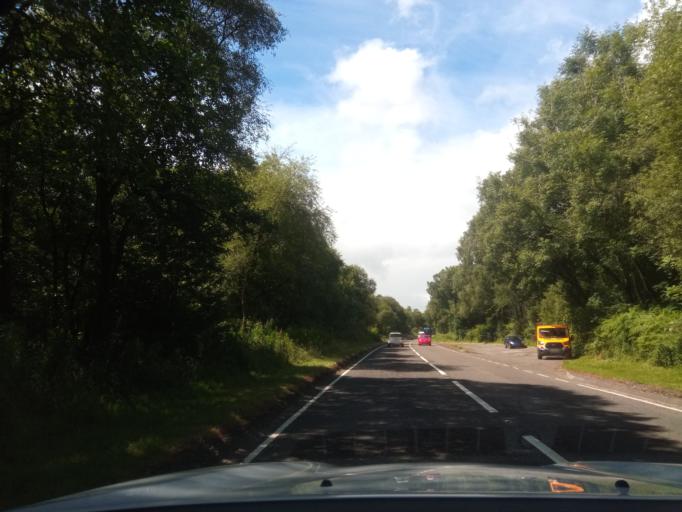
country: GB
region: Scotland
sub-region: Stirling
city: Callander
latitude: 56.2150
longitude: -4.1467
